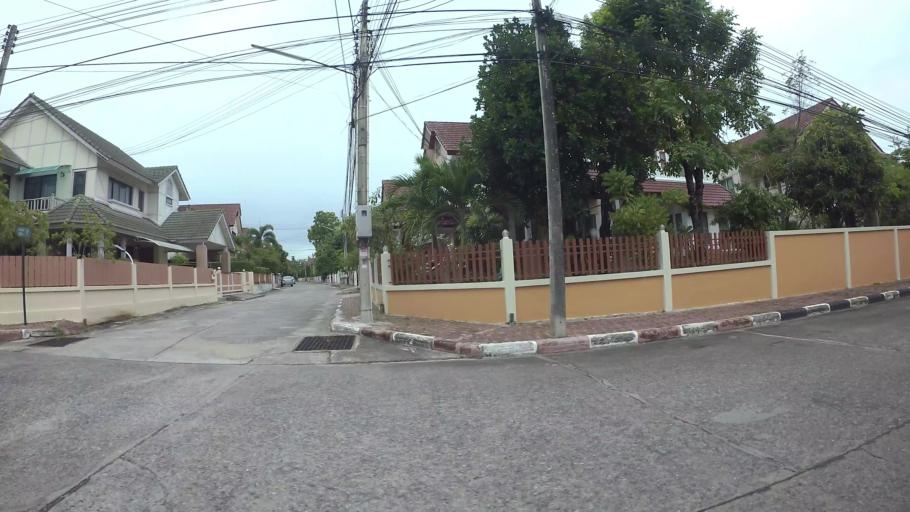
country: TH
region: Chon Buri
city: Si Racha
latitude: 13.1483
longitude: 100.9830
